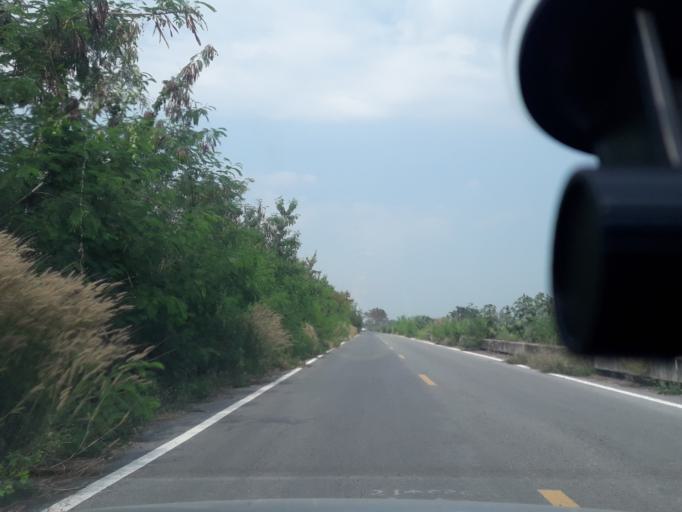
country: TH
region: Sara Buri
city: Nong Khae
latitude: 14.2664
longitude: 100.8913
